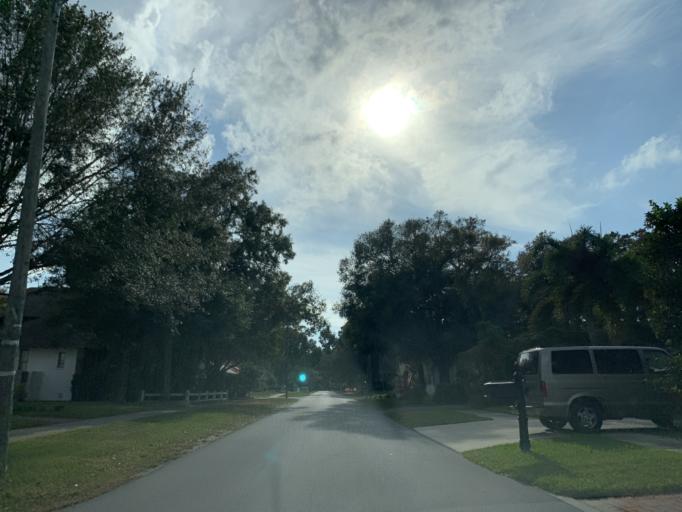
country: US
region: Florida
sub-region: Hillsborough County
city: Tampa
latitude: 27.9066
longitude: -82.4995
